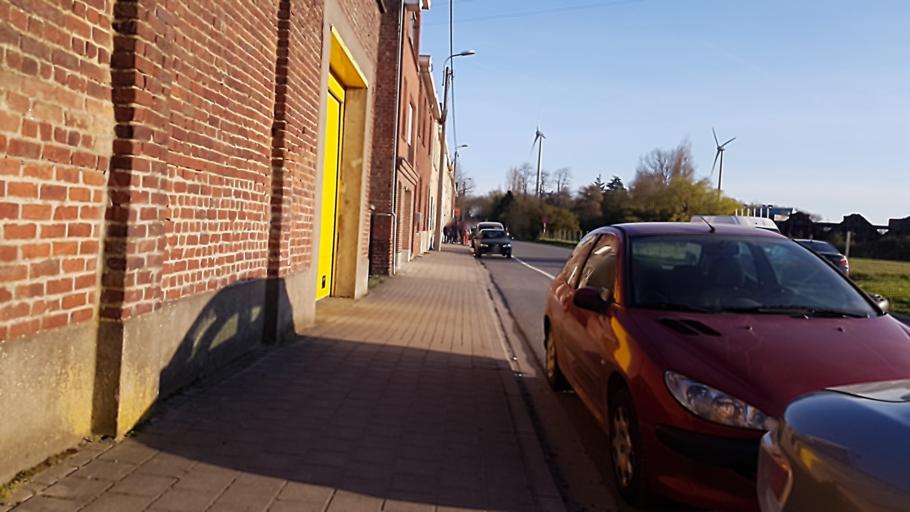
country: BE
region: Flanders
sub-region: Provincie West-Vlaanderen
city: Harelbeke
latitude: 50.8275
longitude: 3.3041
